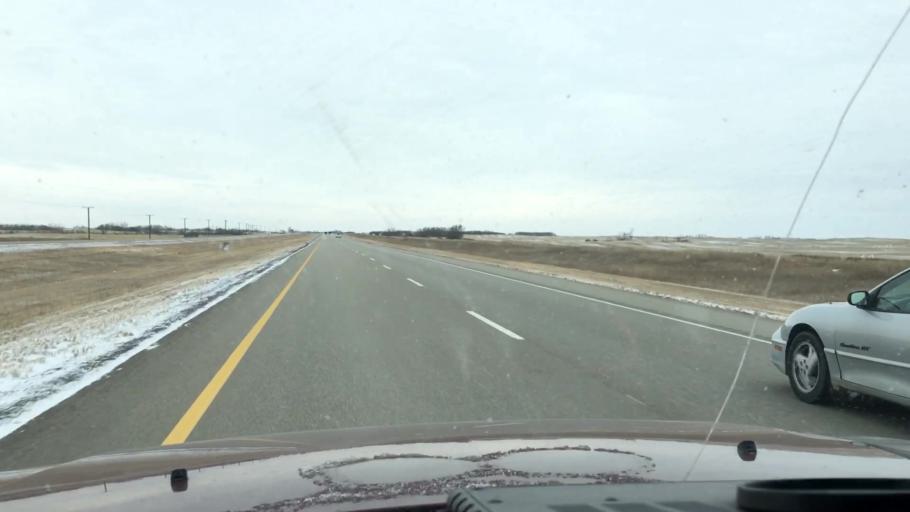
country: CA
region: Saskatchewan
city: Watrous
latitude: 51.4008
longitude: -106.1770
